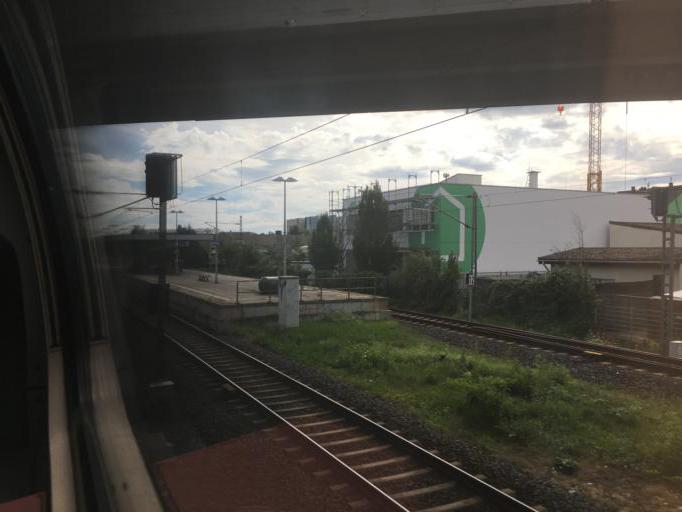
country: DE
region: Hesse
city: Langen
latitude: 50.0066
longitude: 8.6590
